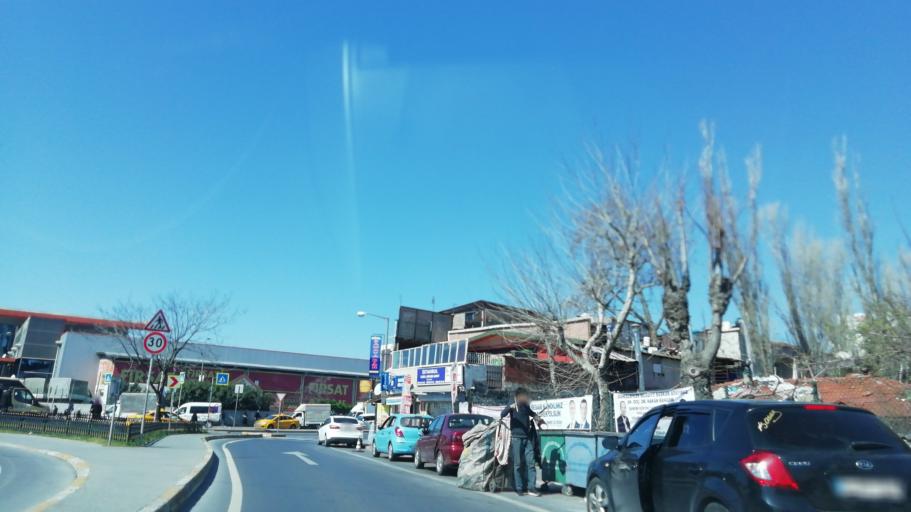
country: TR
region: Istanbul
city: Bahcelievler
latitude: 40.9934
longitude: 28.8361
